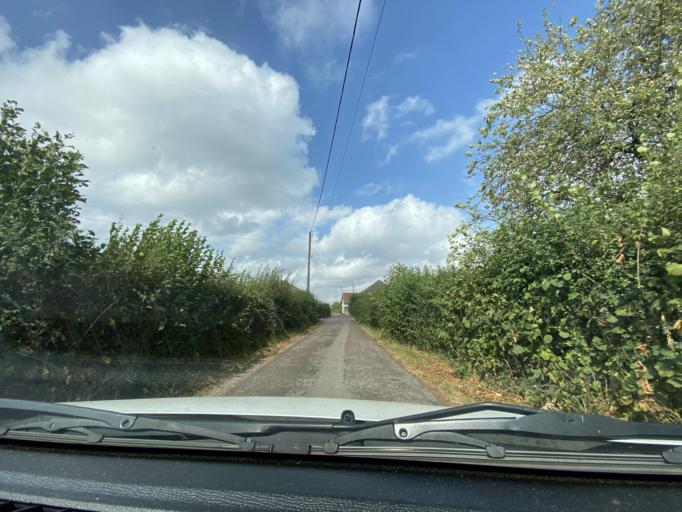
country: FR
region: Bourgogne
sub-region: Departement de la Cote-d'Or
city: Saulieu
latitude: 47.3003
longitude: 4.2373
